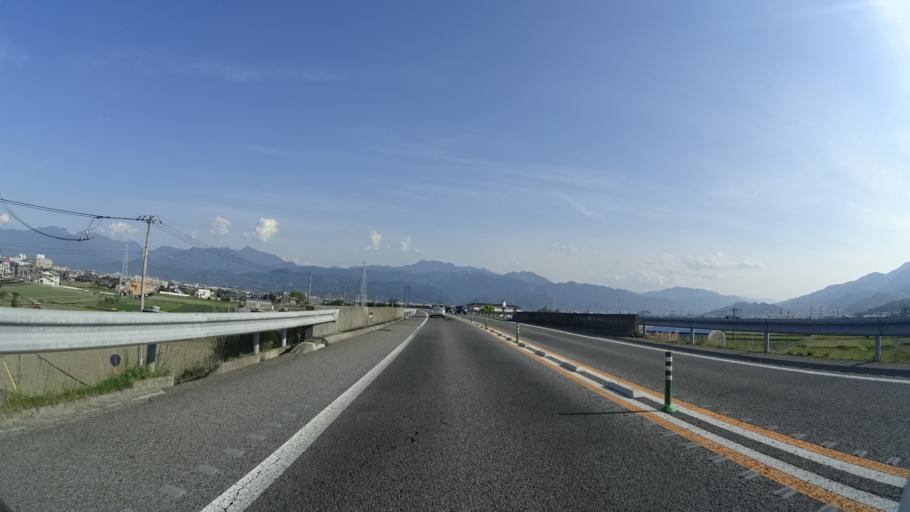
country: JP
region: Ehime
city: Saijo
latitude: 33.9360
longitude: 133.0694
